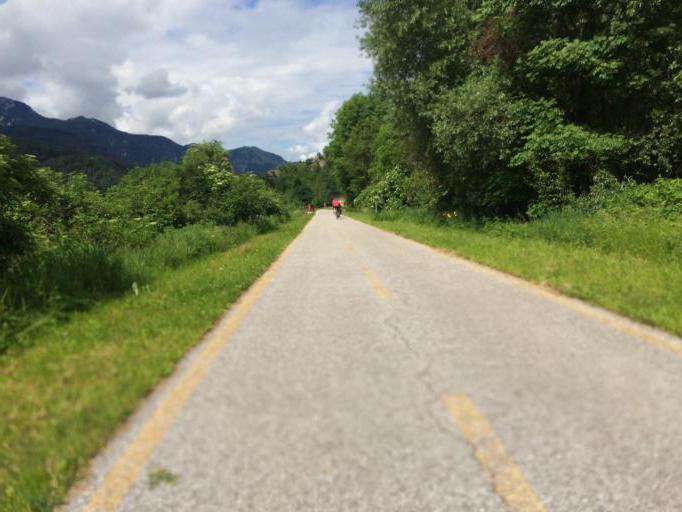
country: IT
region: Friuli Venezia Giulia
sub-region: Provincia di Udine
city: Malborghetto
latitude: 46.5087
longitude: 13.4620
